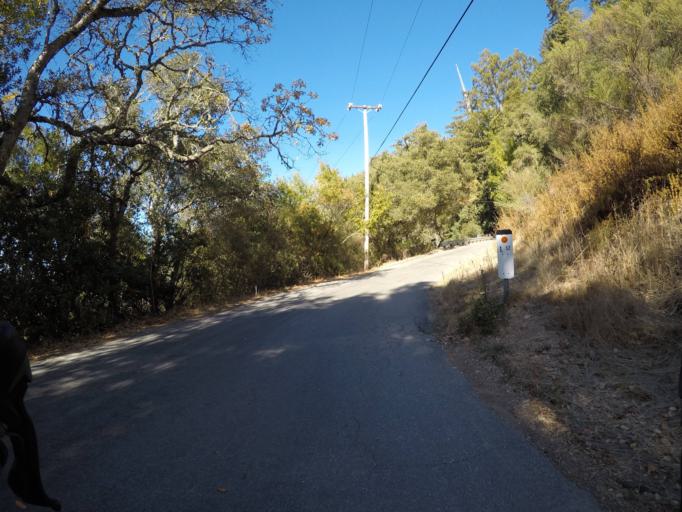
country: US
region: California
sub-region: Santa Clara County
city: Lexington Hills
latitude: 37.1321
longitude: -121.9878
